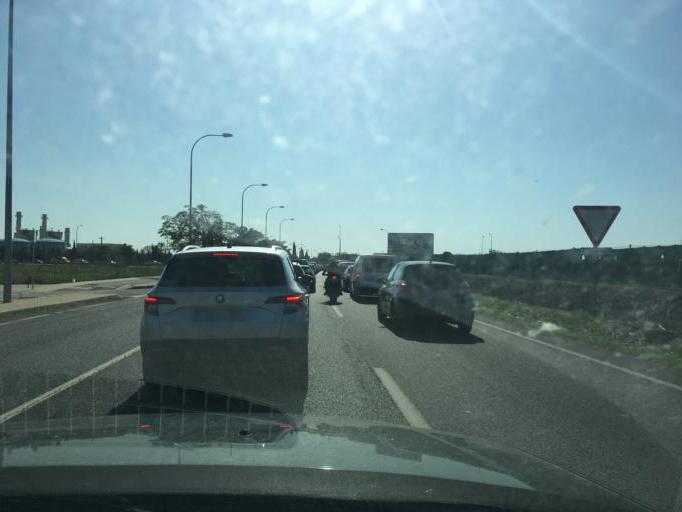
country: ES
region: Balearic Islands
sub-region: Illes Balears
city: Palma
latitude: 39.5722
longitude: 2.6857
